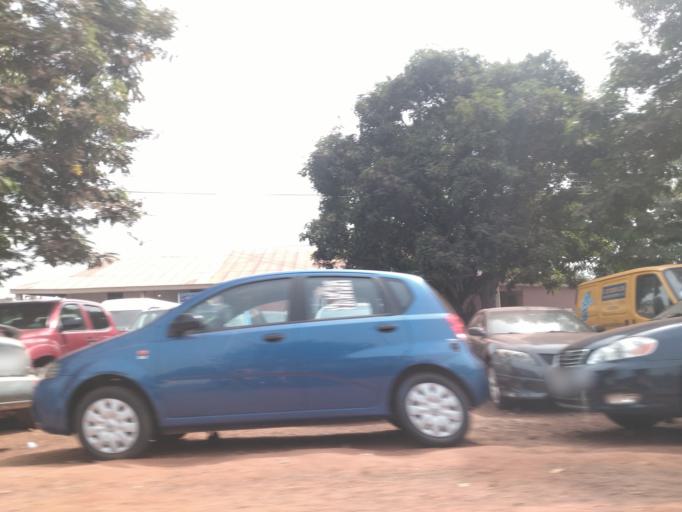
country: GH
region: Ashanti
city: Kumasi
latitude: 6.7096
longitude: -1.6332
